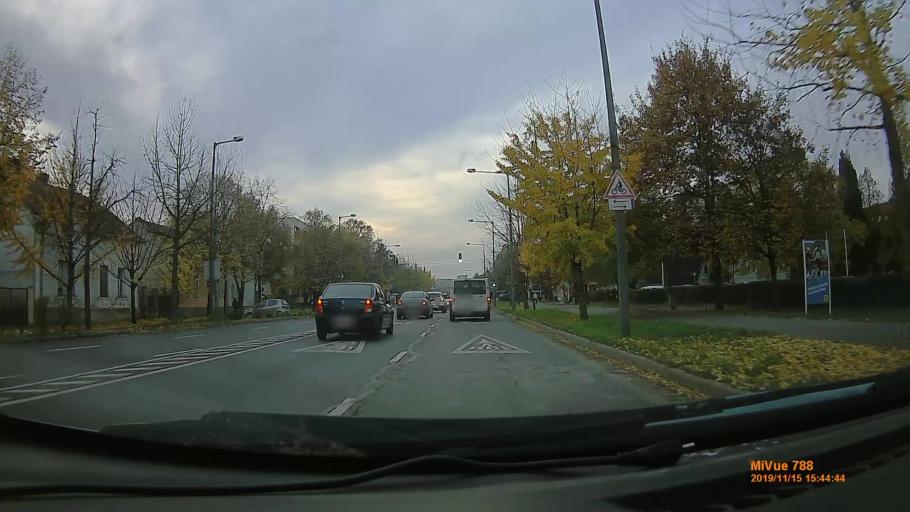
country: HU
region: Bekes
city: Bekescsaba
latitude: 46.6821
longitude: 21.1056
